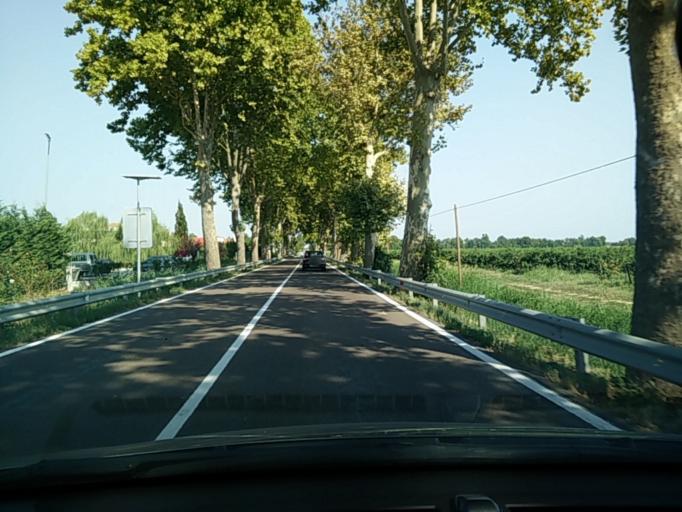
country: IT
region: Veneto
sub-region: Provincia di Venezia
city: San Giorgio di Livenza
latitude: 45.6470
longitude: 12.7794
